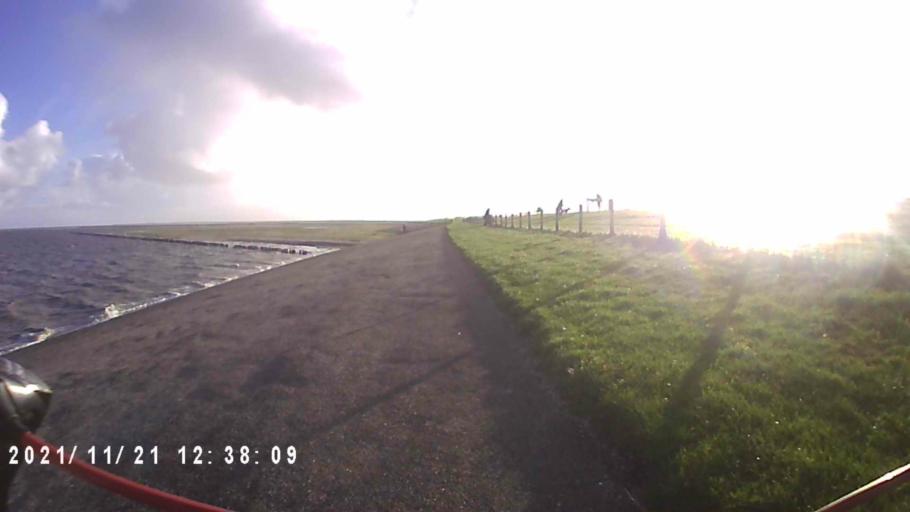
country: NL
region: Friesland
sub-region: Gemeente Dongeradeel
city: Anjum
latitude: 53.4058
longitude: 6.0756
